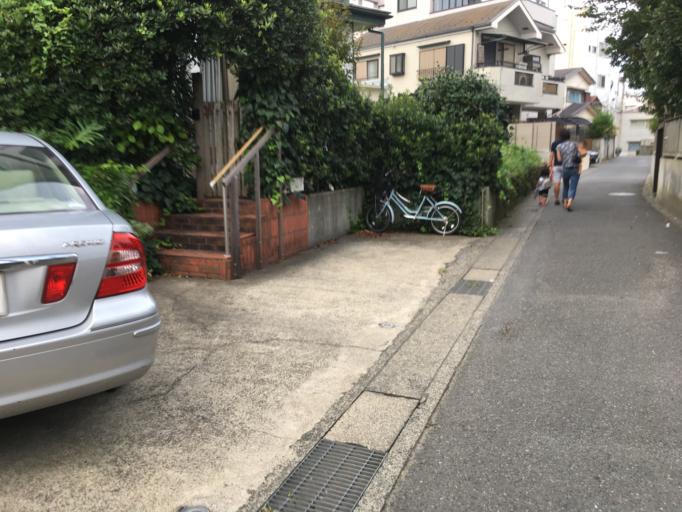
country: JP
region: Kanagawa
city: Kamakura
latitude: 35.3134
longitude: 139.5430
